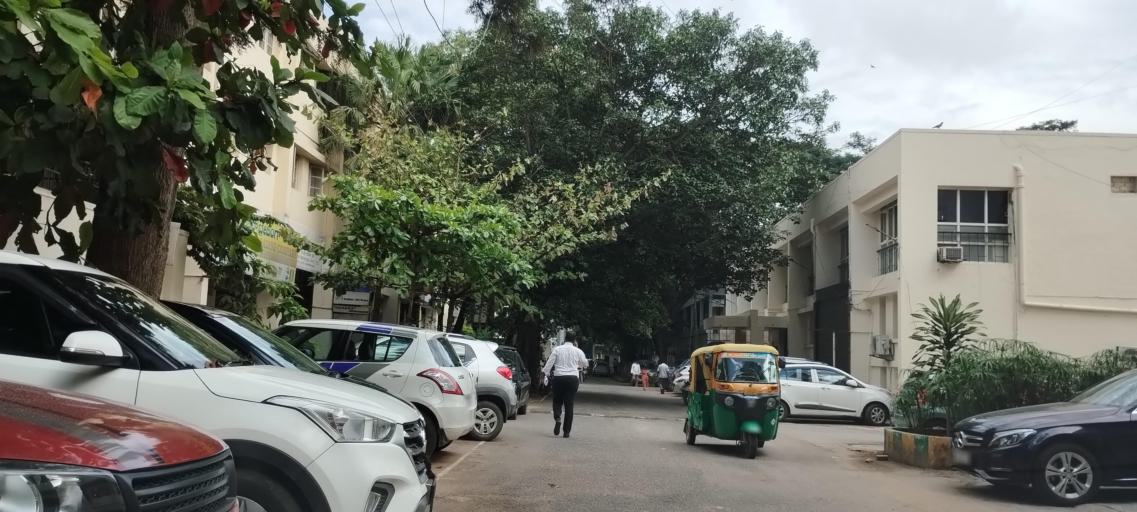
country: IN
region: Karnataka
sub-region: Bangalore Urban
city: Bangalore
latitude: 12.9639
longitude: 77.5867
